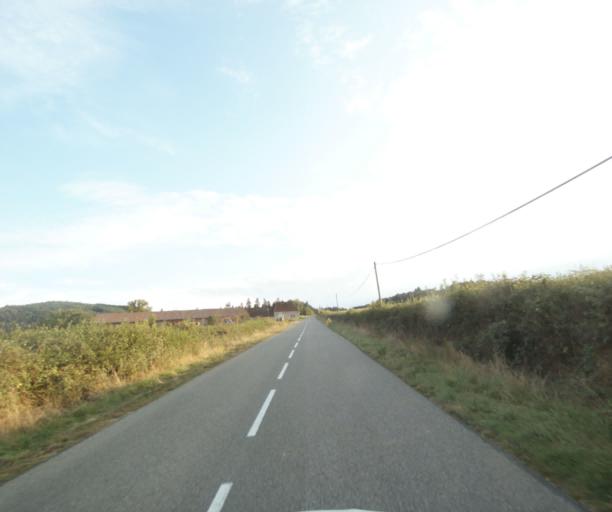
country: FR
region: Bourgogne
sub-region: Departement de Saone-et-Loire
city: Charolles
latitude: 46.4238
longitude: 4.4046
